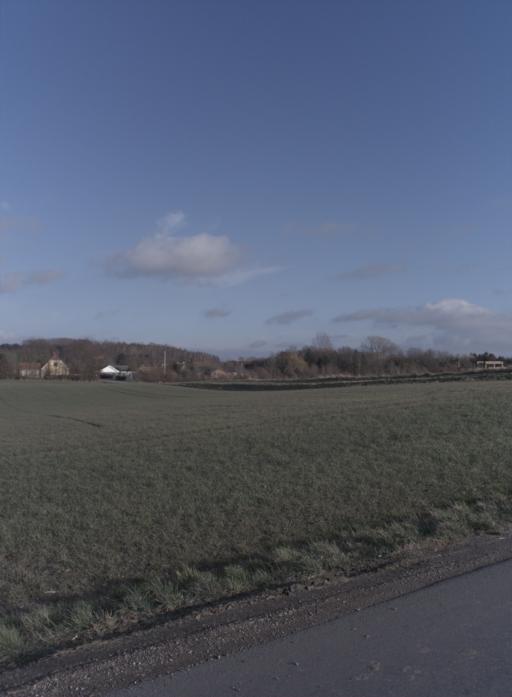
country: DK
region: Zealand
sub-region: Kalundborg Kommune
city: Kalundborg
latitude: 55.6871
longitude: 11.1305
